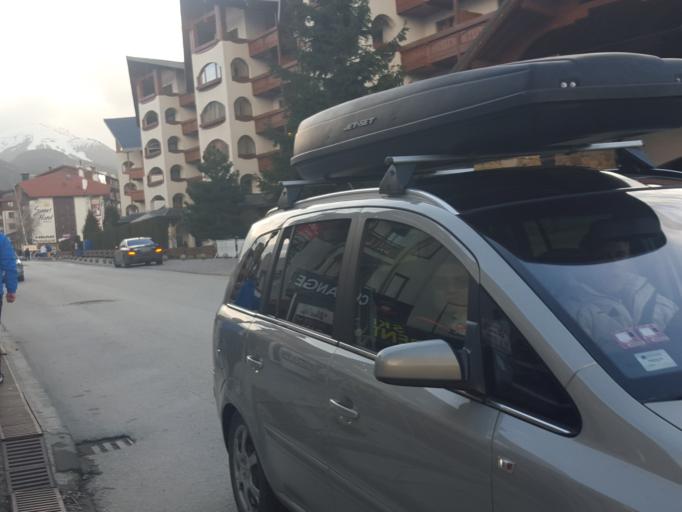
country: BG
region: Blagoevgrad
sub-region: Obshtina Bansko
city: Bansko
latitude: 41.8267
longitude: 23.4788
